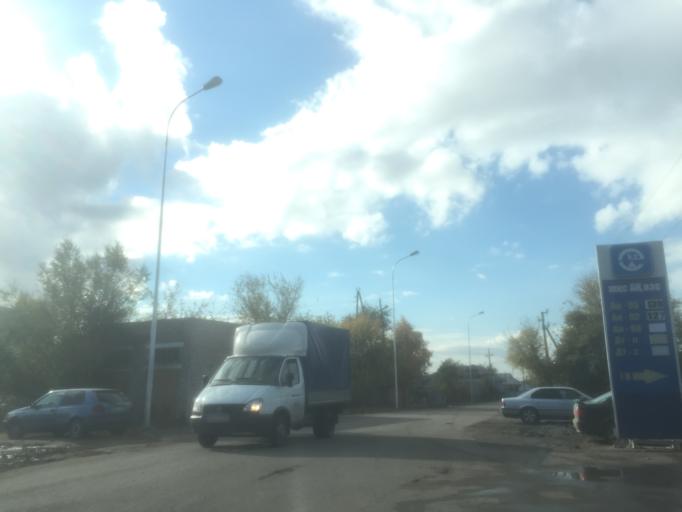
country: KZ
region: Astana Qalasy
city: Astana
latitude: 51.1936
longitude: 71.4009
